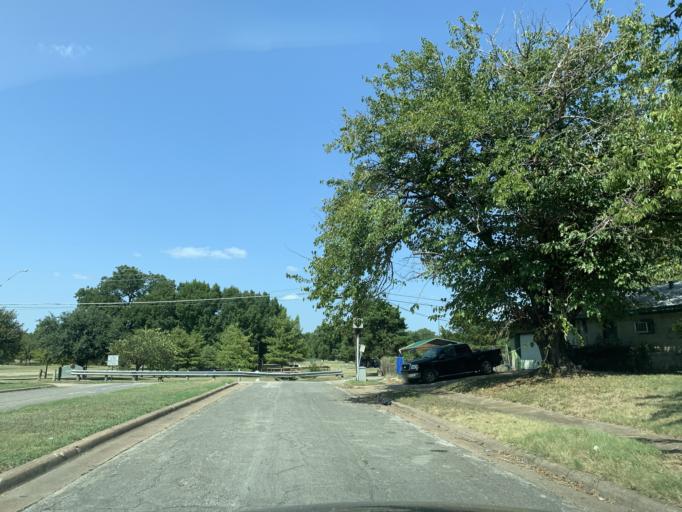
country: US
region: Texas
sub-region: Dallas County
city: Hutchins
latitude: 32.6788
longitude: -96.7962
